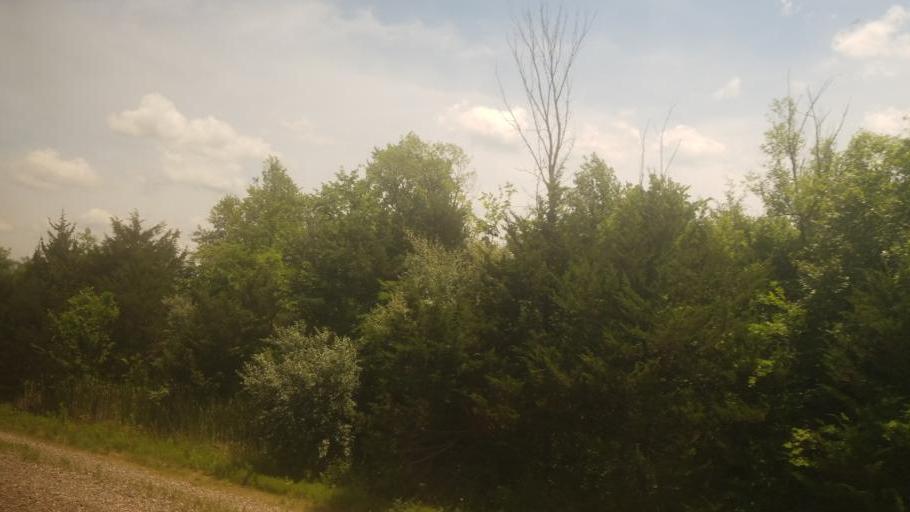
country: US
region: Missouri
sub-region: Macon County
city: La Plata
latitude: 40.0314
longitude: -92.4846
